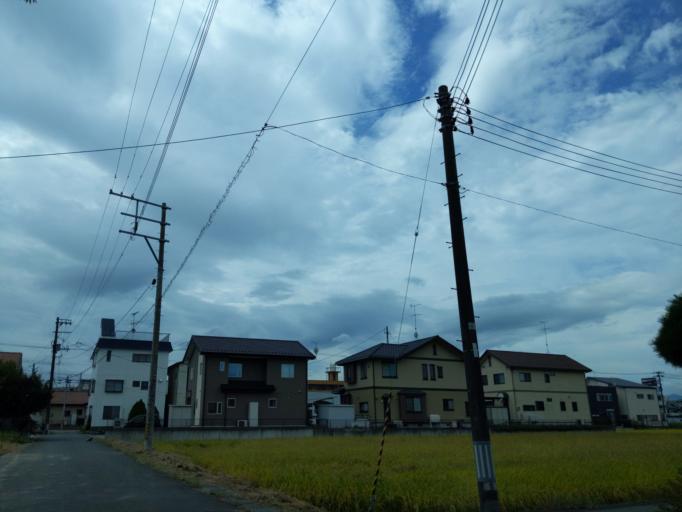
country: JP
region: Fukushima
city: Koriyama
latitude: 37.3943
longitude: 140.3999
